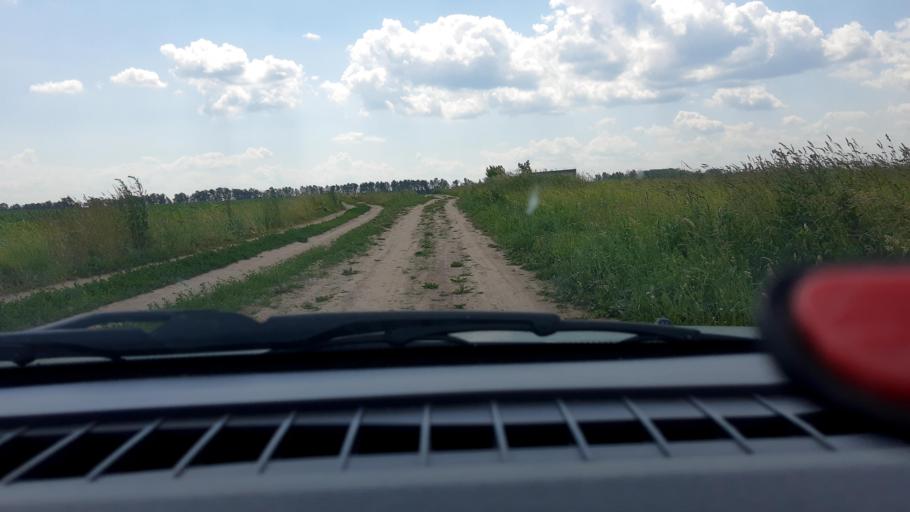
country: RU
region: Nizjnij Novgorod
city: Afonino
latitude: 56.1257
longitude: 44.0316
